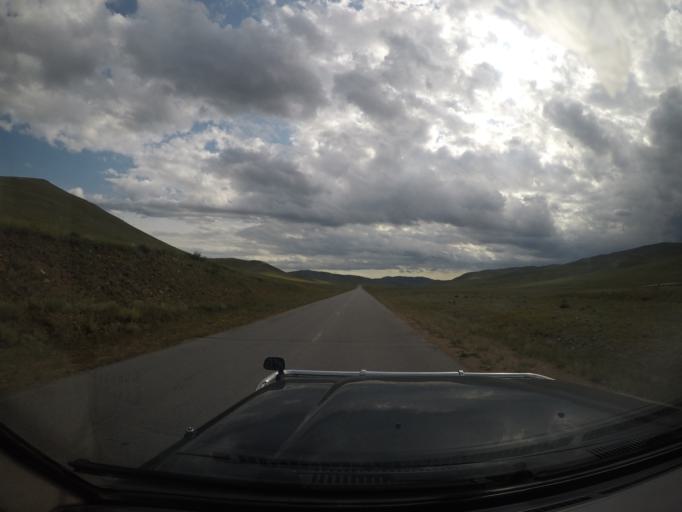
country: MN
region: Hentiy
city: Modot
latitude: 47.7250
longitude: 108.5857
